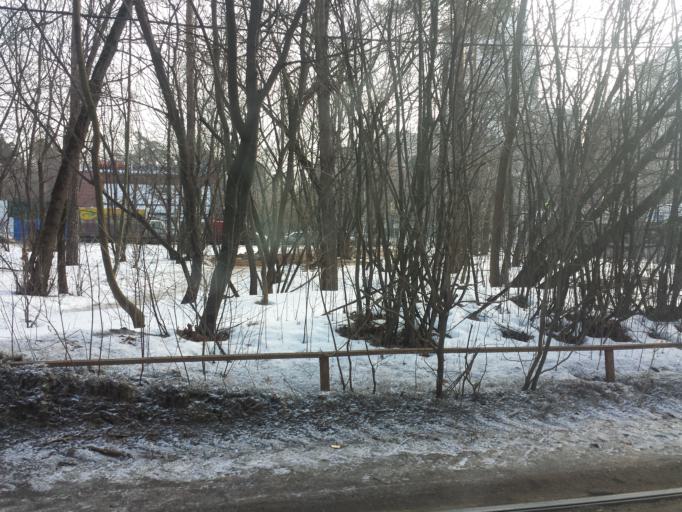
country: RU
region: Moscow
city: Pokrovskoye-Streshnevo
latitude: 55.8107
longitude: 37.4751
